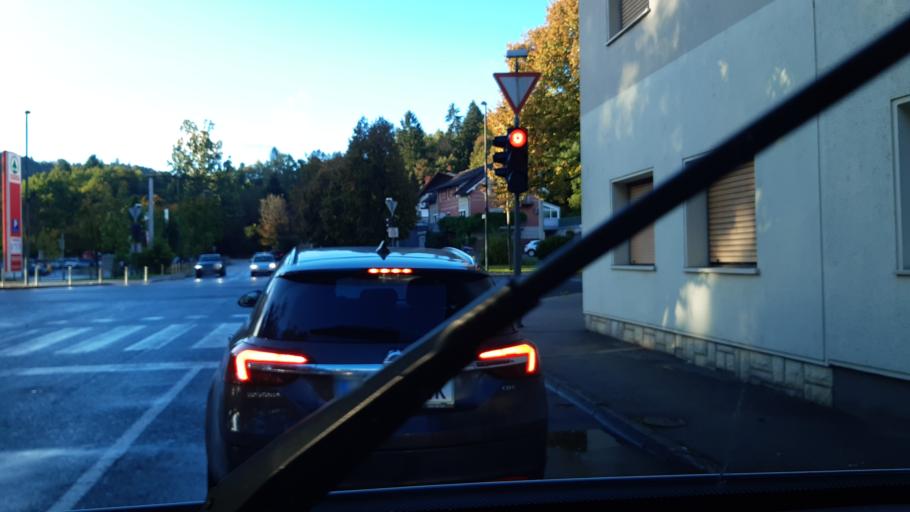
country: SI
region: Ljubljana
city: Ljubljana
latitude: 46.0481
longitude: 14.5430
